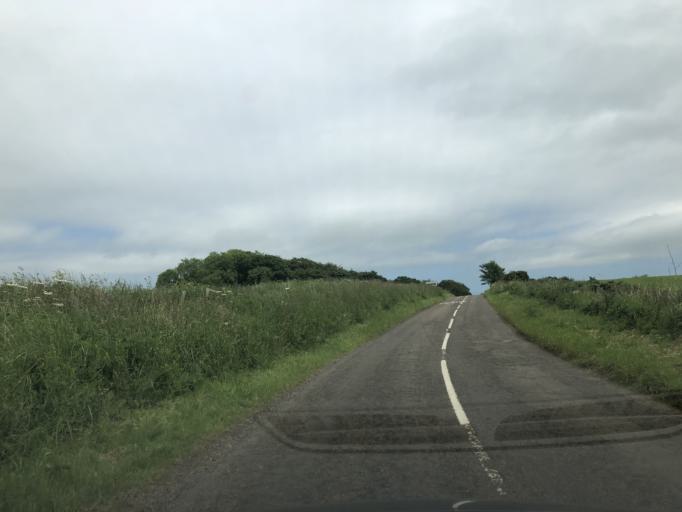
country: GB
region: Scotland
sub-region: Angus
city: Brechin
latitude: 56.7372
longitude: -2.7186
